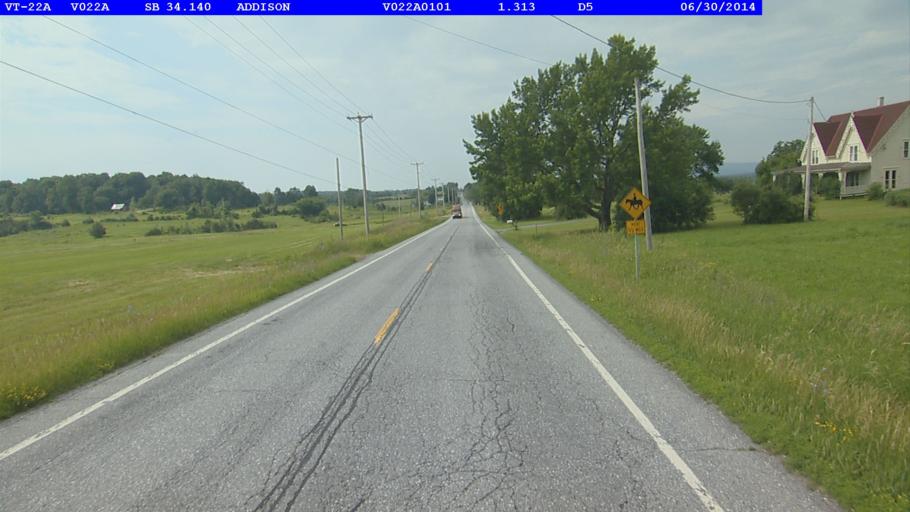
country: US
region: Vermont
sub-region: Addison County
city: Vergennes
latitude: 44.0486
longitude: -73.3028
